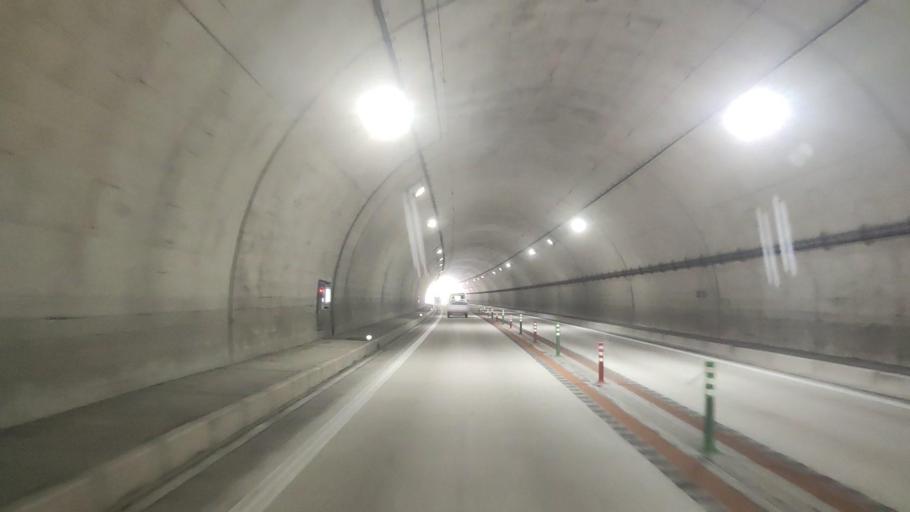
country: JP
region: Wakayama
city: Tanabe
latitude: 33.5842
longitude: 135.4498
